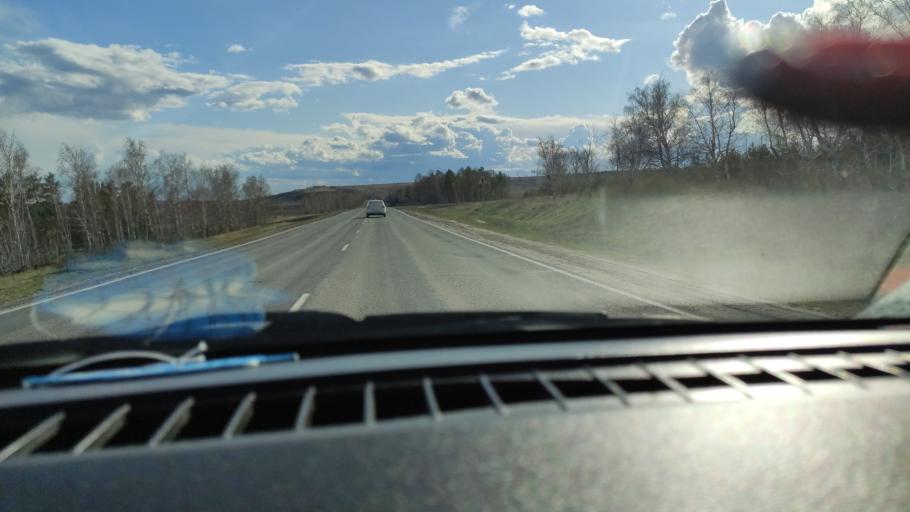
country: RU
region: Saratov
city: Sennoy
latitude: 52.1074
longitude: 46.8241
